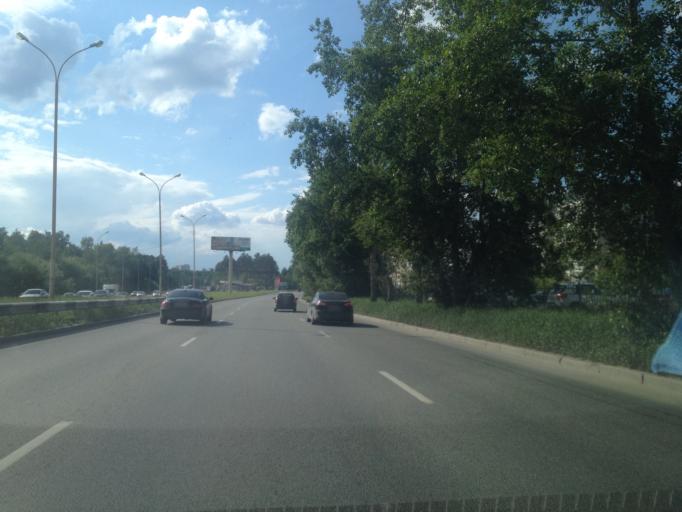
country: RU
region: Sverdlovsk
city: Sovkhoznyy
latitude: 56.8002
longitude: 60.5505
